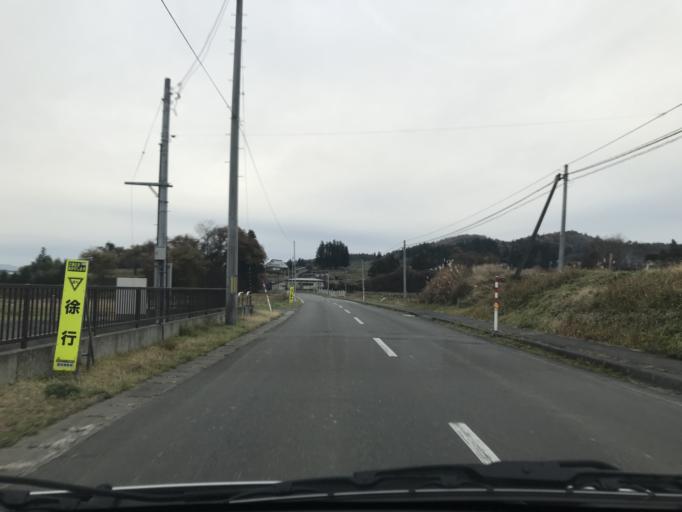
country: JP
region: Iwate
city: Kitakami
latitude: 39.2799
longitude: 141.2661
